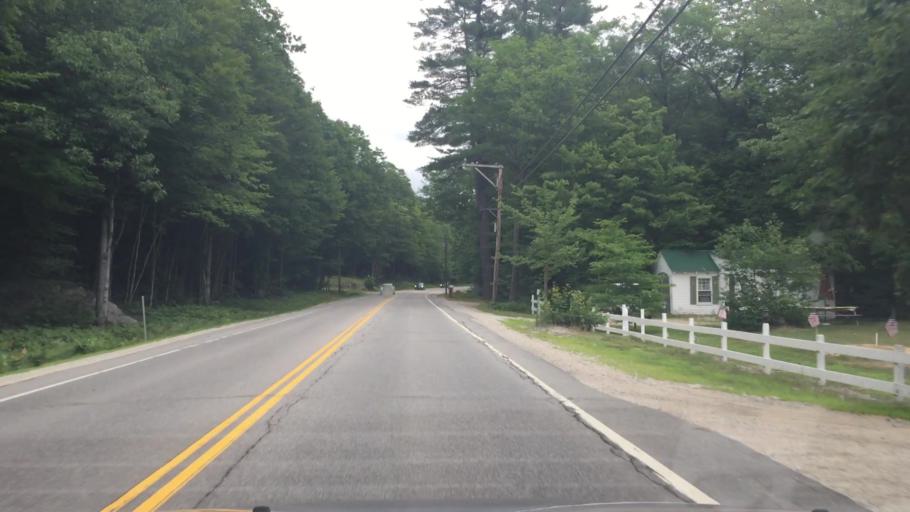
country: US
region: New Hampshire
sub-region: Carroll County
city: Conway
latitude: 43.9596
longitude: -71.1854
